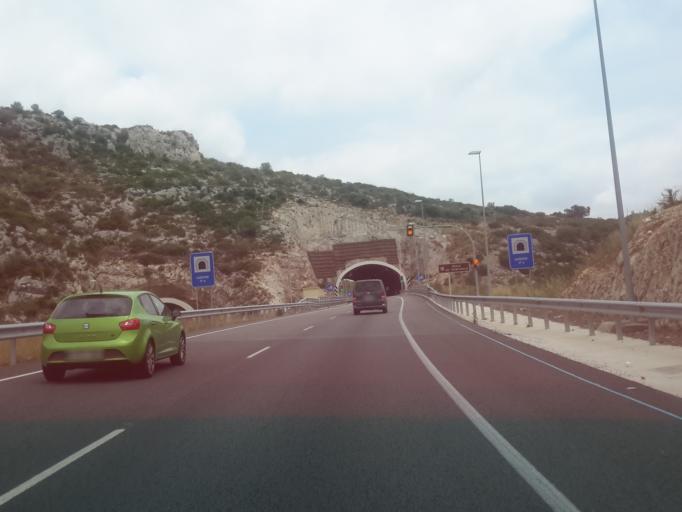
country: ES
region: Catalonia
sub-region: Provincia de Barcelona
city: Vilafranca del Penedes
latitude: 41.3063
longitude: 1.7217
